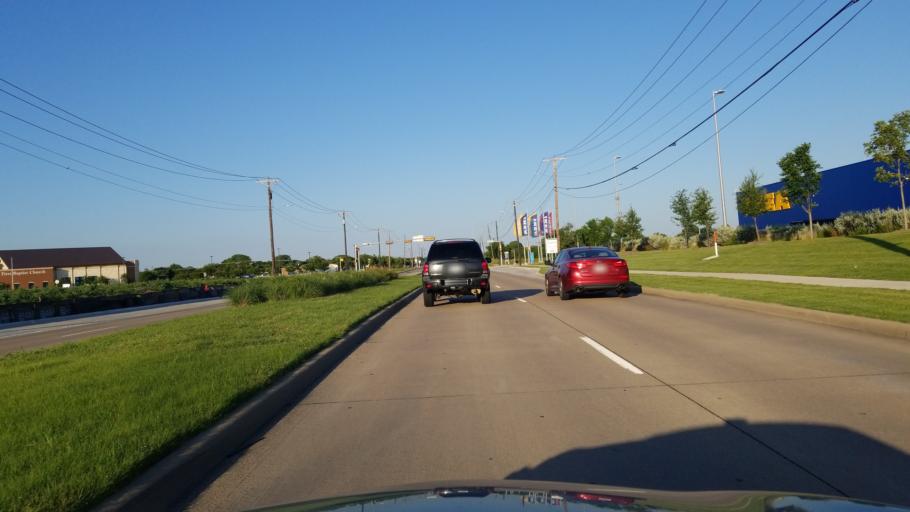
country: US
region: Texas
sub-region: Dallas County
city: Grand Prairie
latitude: 32.6917
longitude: -97.0223
